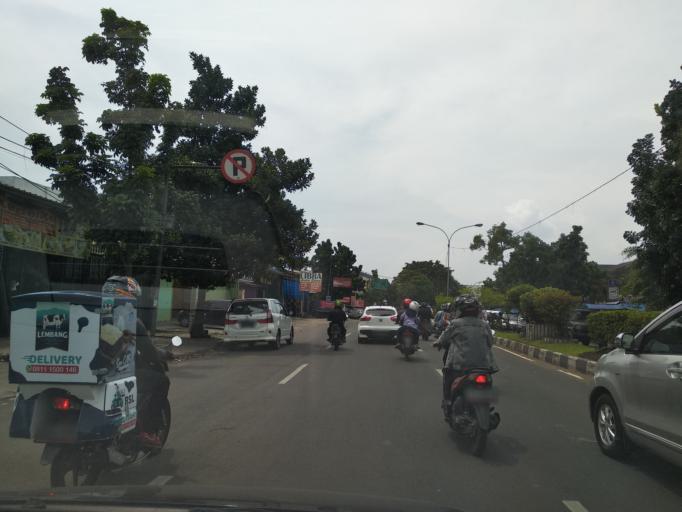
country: ID
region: West Java
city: Bandung
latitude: -6.9373
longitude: 107.6006
